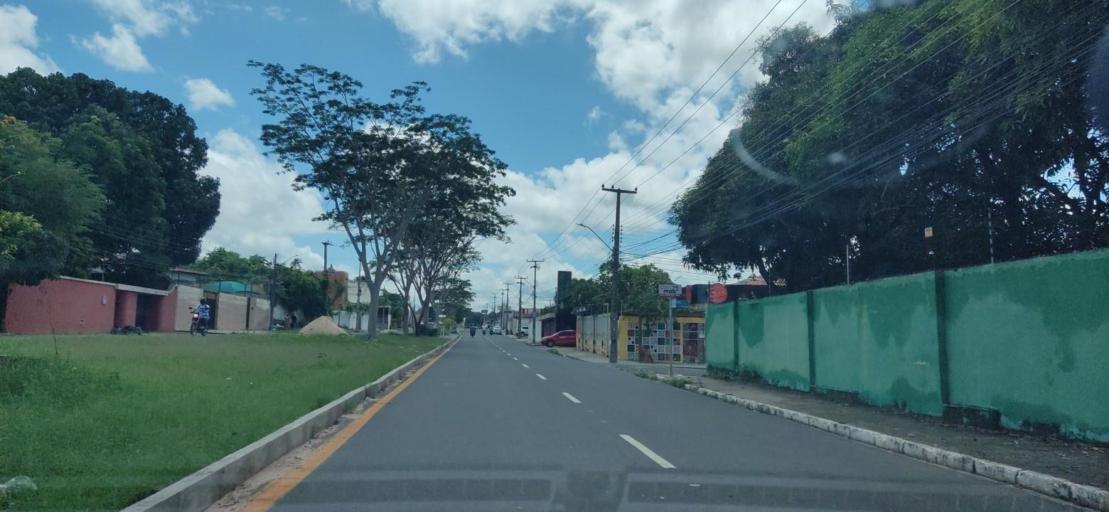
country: BR
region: Piaui
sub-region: Teresina
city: Teresina
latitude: -5.0650
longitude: -42.7678
